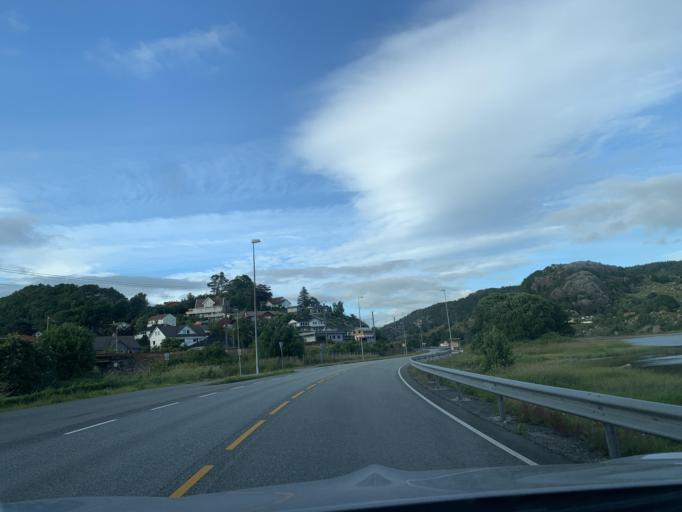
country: NO
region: Rogaland
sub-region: Eigersund
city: Egersund
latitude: 58.4623
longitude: 6.0176
